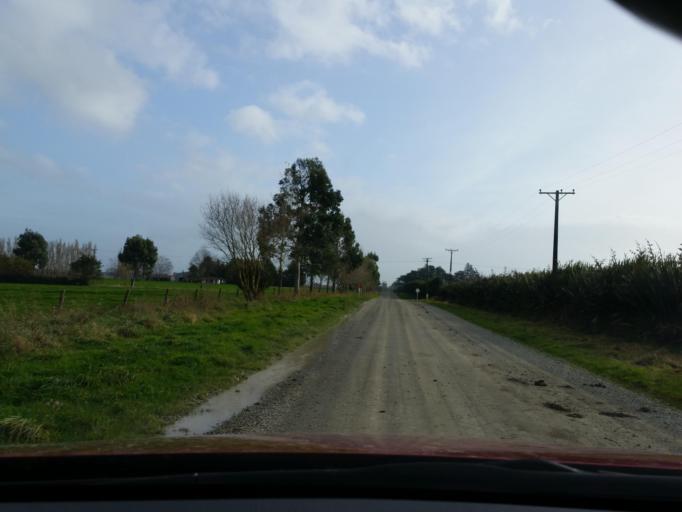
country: NZ
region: Southland
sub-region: Southland District
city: Winton
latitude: -46.2268
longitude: 168.3213
